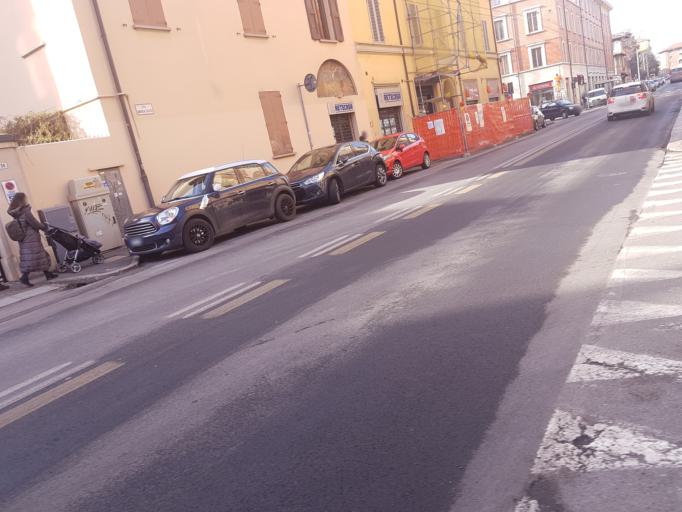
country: IT
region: Emilia-Romagna
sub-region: Provincia di Bologna
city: Bologna
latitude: 44.4951
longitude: 11.3255
